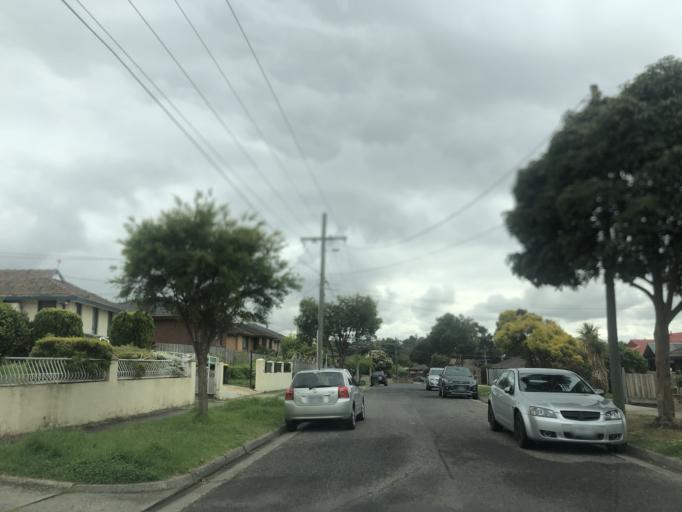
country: AU
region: Victoria
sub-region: Greater Dandenong
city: Dandenong North
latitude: -37.9595
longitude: 145.2210
